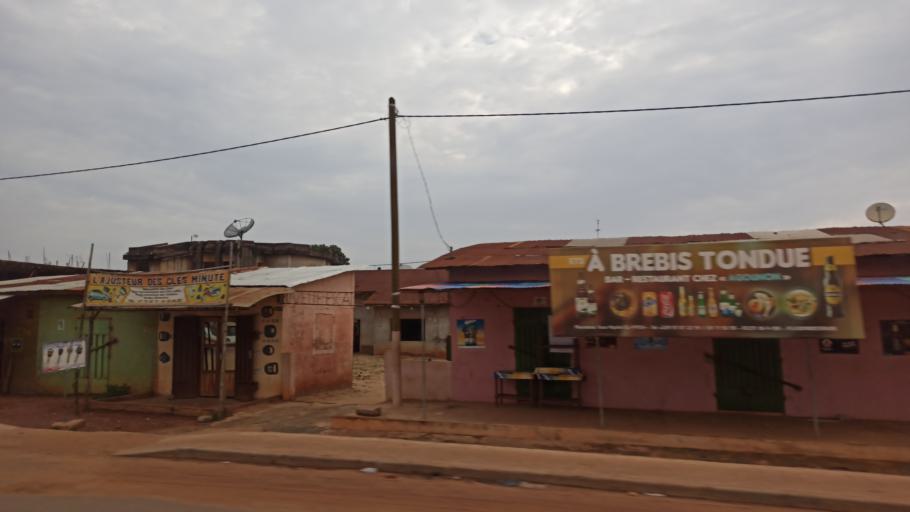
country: BJ
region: Queme
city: Porto-Novo
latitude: 6.5176
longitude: 2.6037
